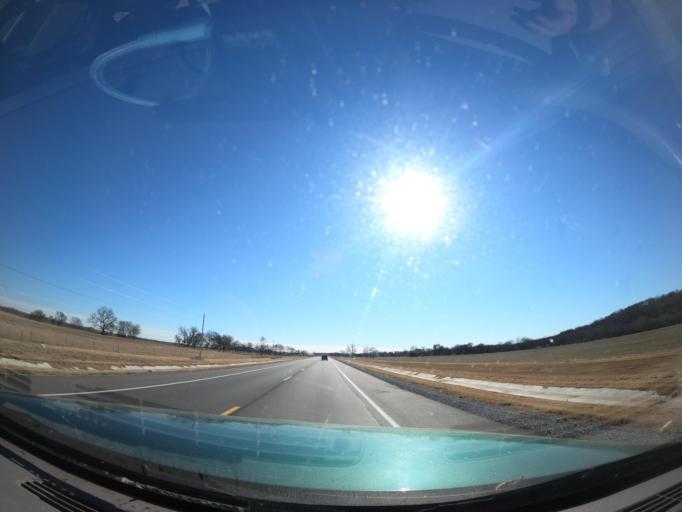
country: US
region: Oklahoma
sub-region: Wagoner County
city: Coweta
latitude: 35.8968
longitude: -95.6592
